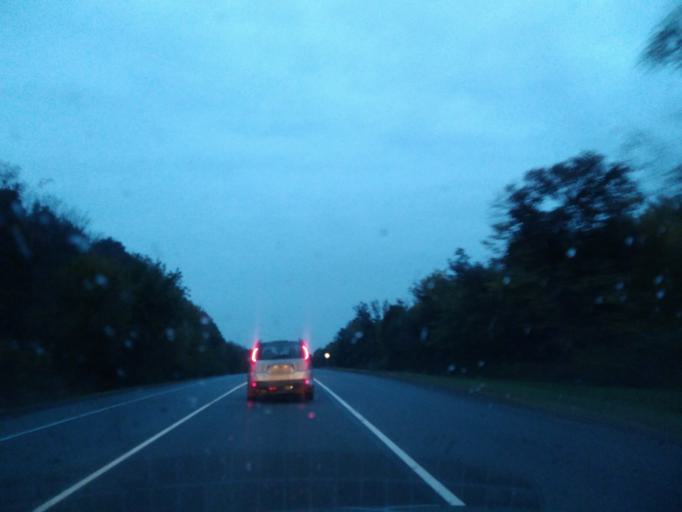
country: RU
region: Tula
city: Shchekino
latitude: 53.8877
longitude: 37.4517
